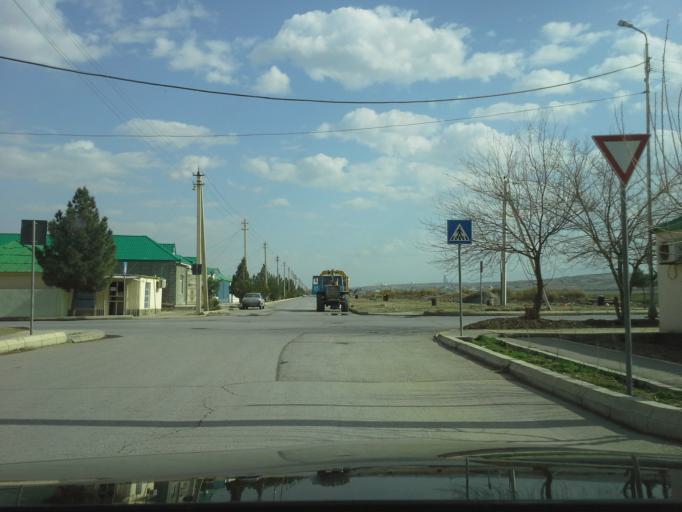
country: TM
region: Ahal
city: Ashgabat
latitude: 37.9858
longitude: 58.2826
